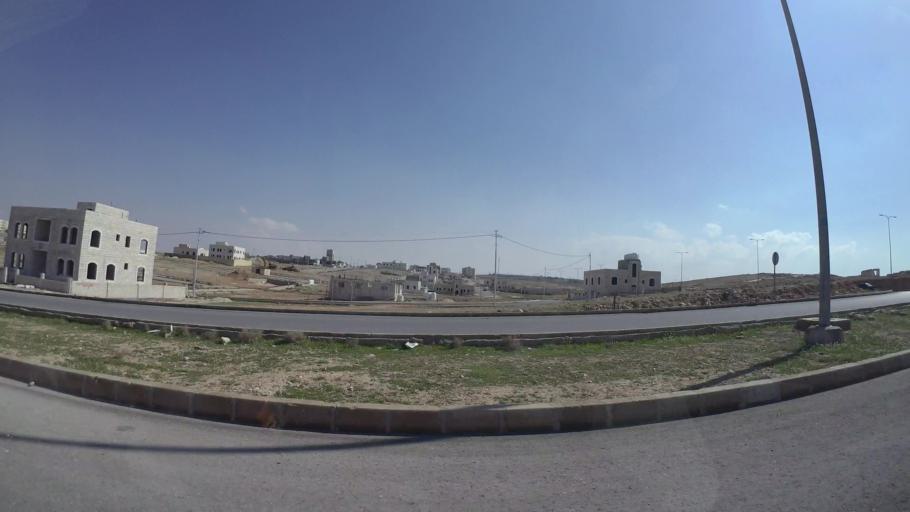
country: JO
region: Zarqa
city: Zarqa
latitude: 32.0540
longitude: 36.1141
